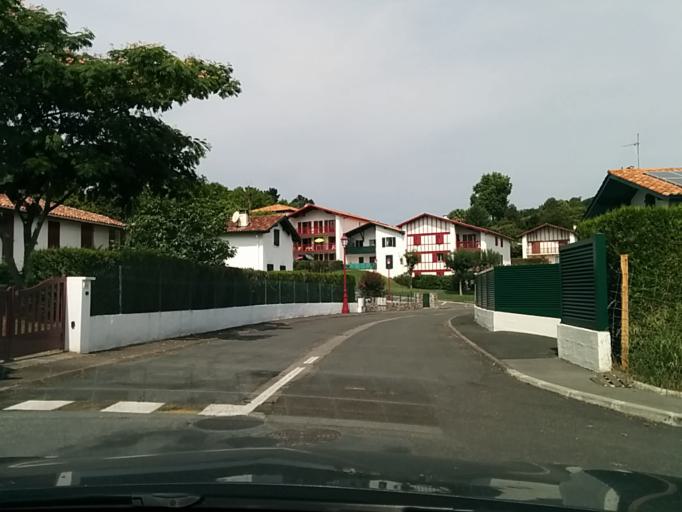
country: FR
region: Aquitaine
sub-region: Departement des Pyrenees-Atlantiques
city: Urrugne
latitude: 43.3641
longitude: -1.7011
